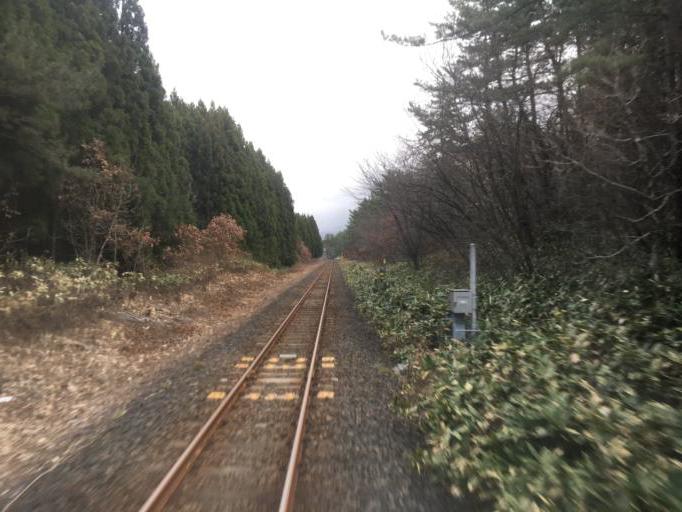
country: JP
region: Aomori
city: Mutsu
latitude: 41.0119
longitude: 141.2406
